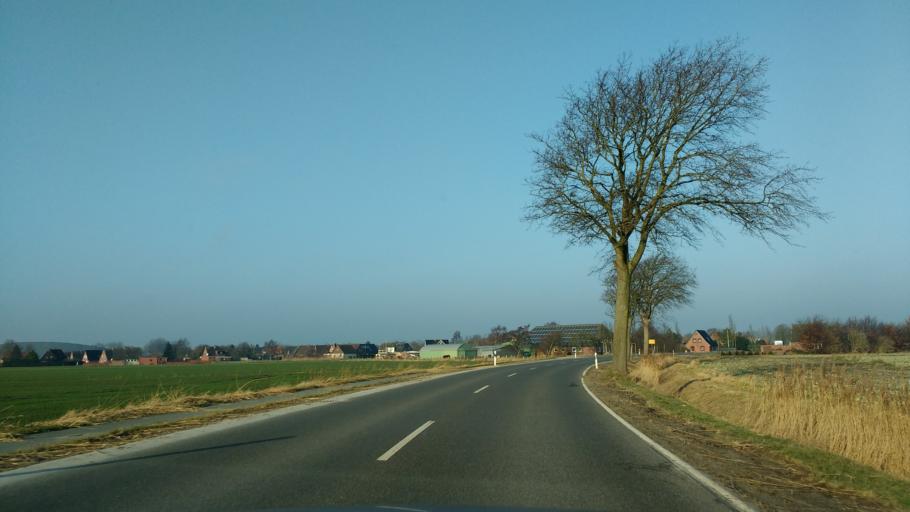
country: DE
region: Schleswig-Holstein
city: Friedrichskoog
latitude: 53.9992
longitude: 8.8880
